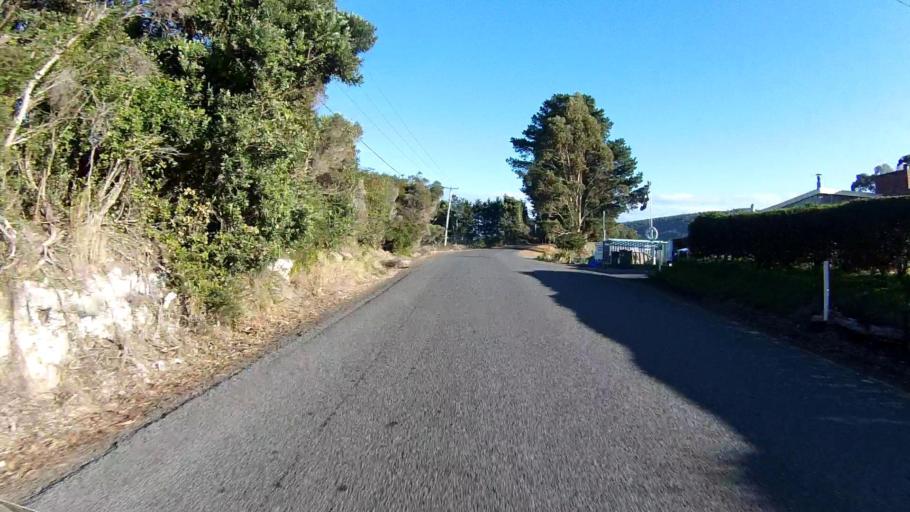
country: AU
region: Tasmania
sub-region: Clarence
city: Sandford
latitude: -43.1681
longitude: 147.8592
